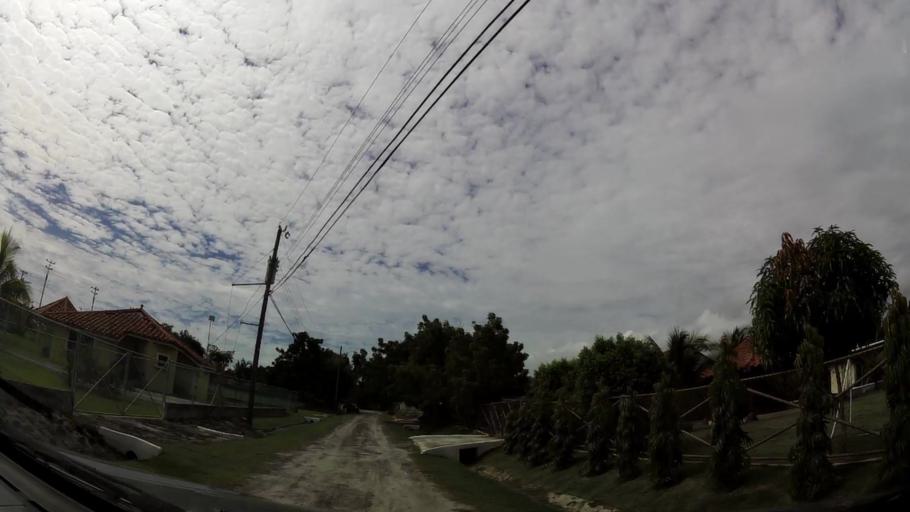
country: PA
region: Panama
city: Nueva Gorgona
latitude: 8.5419
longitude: -79.9078
